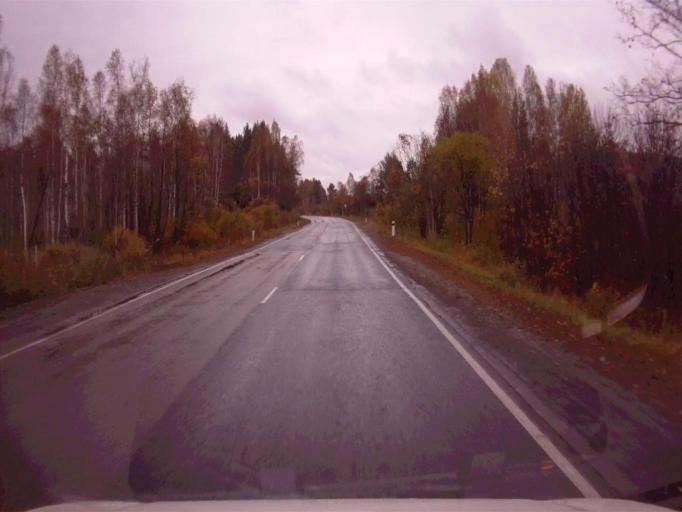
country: RU
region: Chelyabinsk
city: Verkhniy Ufaley
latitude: 55.9940
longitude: 60.3327
